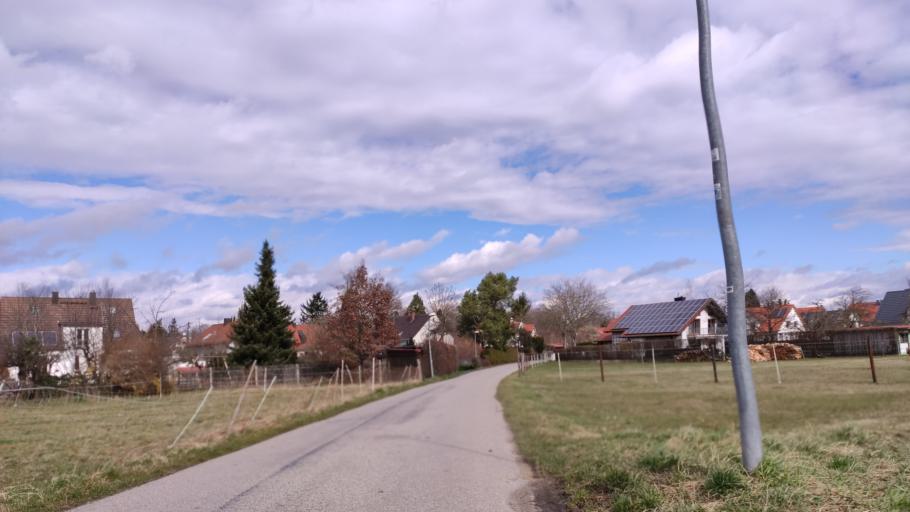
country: DE
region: Bavaria
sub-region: Upper Bavaria
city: Emmering
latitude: 48.1764
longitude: 11.2742
